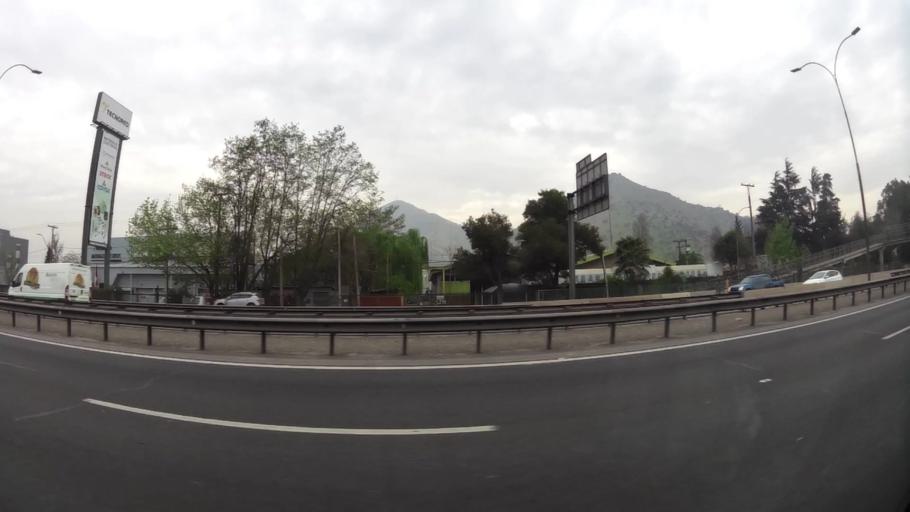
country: CL
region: Santiago Metropolitan
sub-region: Provincia de Santiago
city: Lo Prado
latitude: -33.3838
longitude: -70.6922
